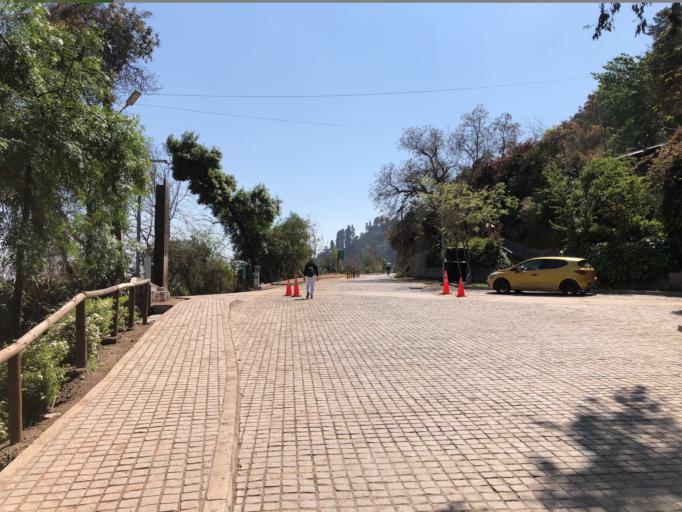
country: CL
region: Santiago Metropolitan
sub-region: Provincia de Santiago
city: Santiago
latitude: -33.4277
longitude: -70.6379
